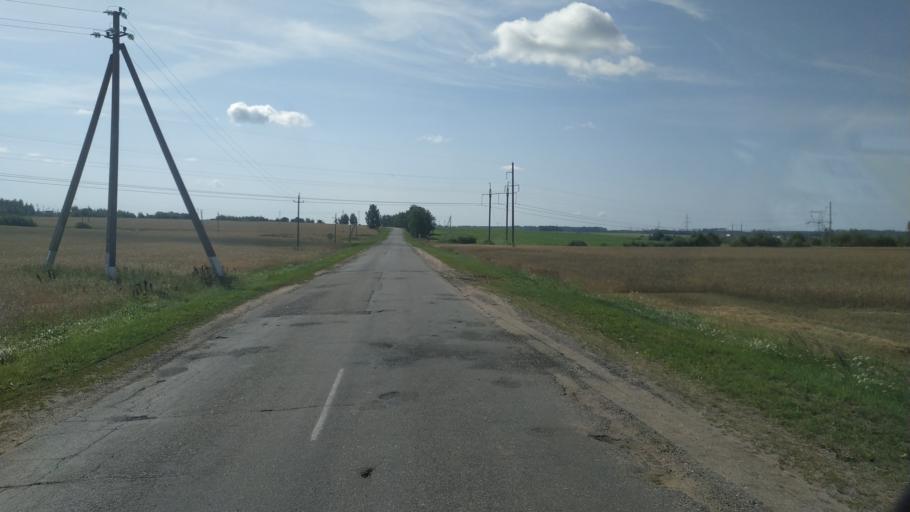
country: BY
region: Mogilev
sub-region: Mahilyowski Rayon
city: Veyno
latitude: 53.7906
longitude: 30.4315
